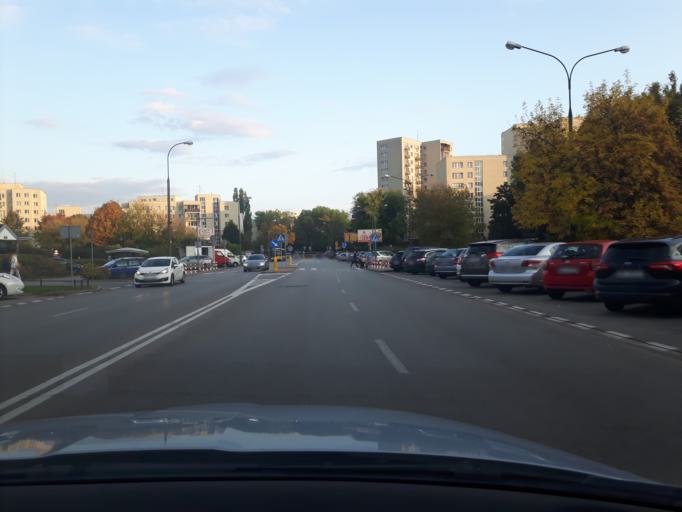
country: PL
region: Masovian Voivodeship
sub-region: Warszawa
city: Ursynow
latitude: 52.1553
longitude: 21.0284
